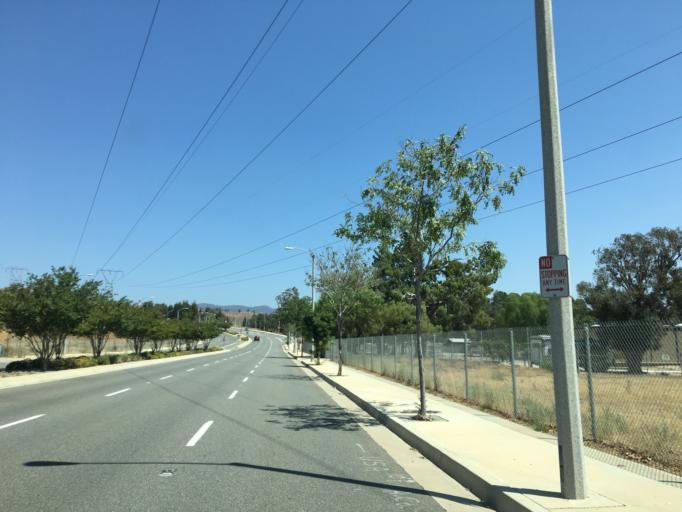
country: US
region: California
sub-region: Los Angeles County
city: Castaic
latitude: 34.4983
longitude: -118.6162
